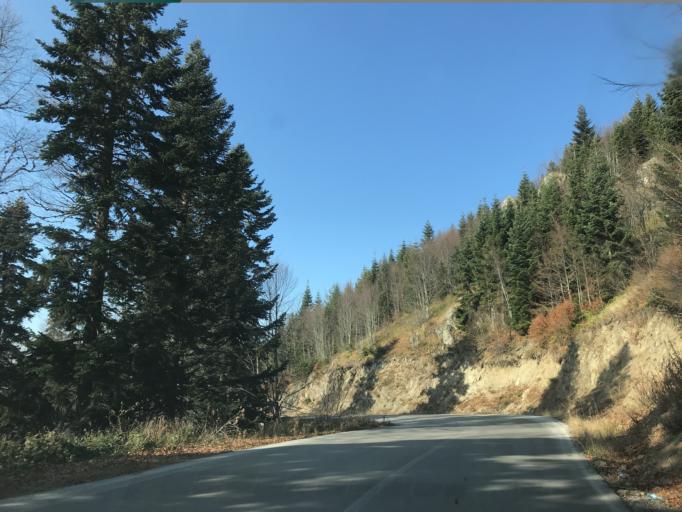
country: TR
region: Bolu
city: Bolu
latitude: 40.8870
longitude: 31.6806
